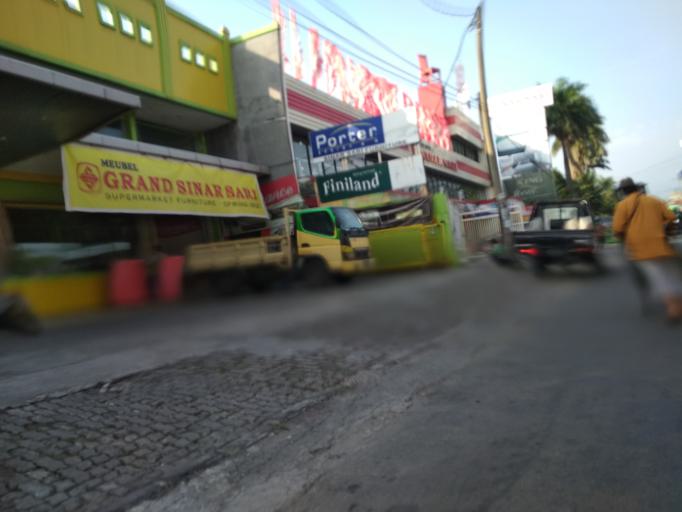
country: ID
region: West Java
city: Bogor
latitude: -6.5916
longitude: 106.7905
